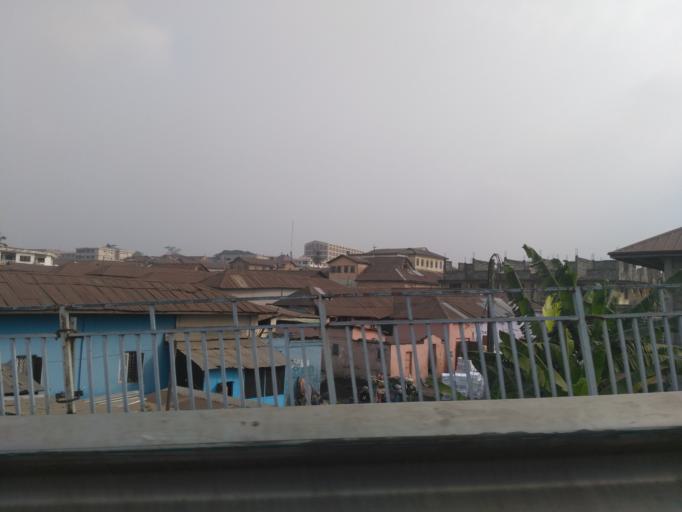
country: GH
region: Ashanti
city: Kumasi
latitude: 6.6896
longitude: -1.6170
